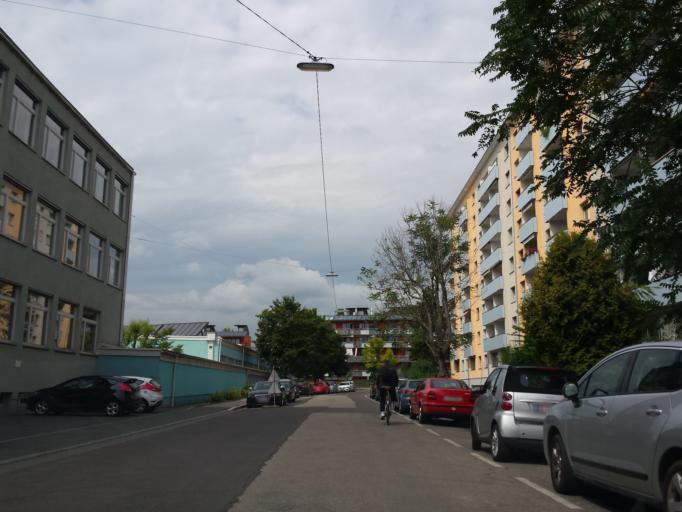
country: AT
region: Styria
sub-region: Graz Stadt
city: Graz
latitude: 47.0878
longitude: 15.4308
